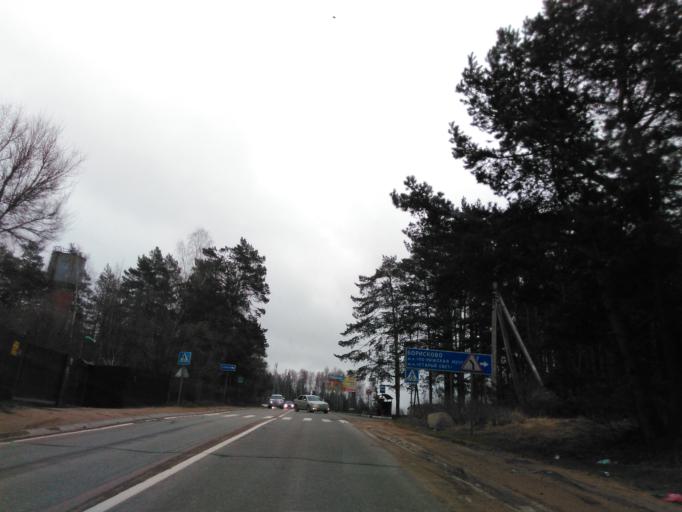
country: RU
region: Moskovskaya
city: Snegiri
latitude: 55.8413
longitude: 36.9660
